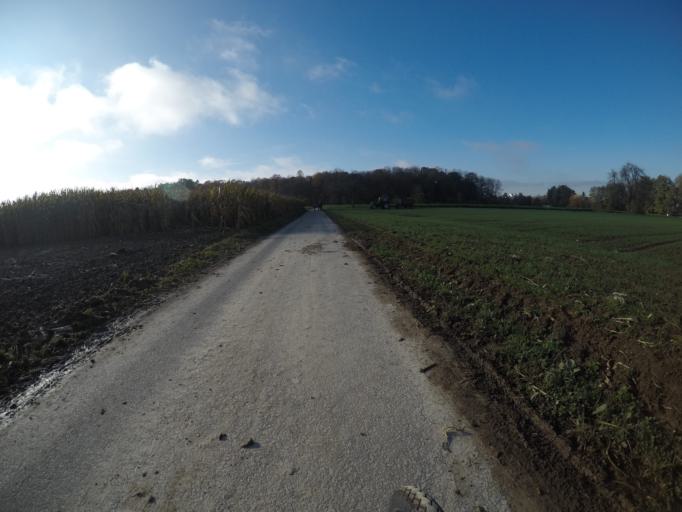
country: DE
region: Baden-Wuerttemberg
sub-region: Regierungsbezirk Stuttgart
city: Leinfelden-Echterdingen
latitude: 48.7129
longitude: 9.1336
